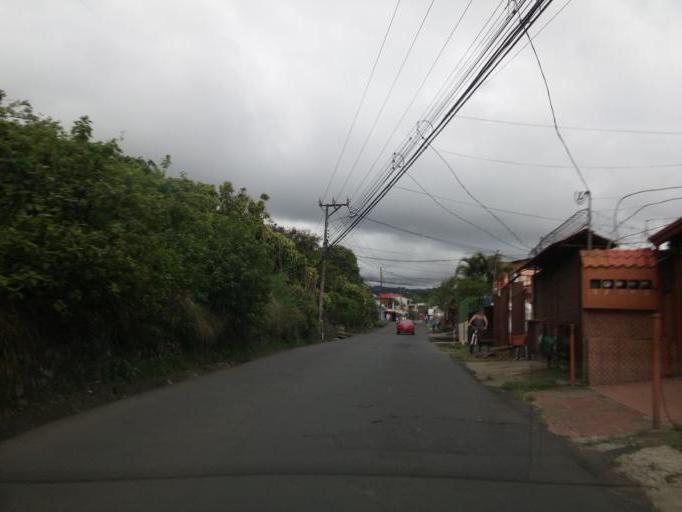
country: CR
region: Heredia
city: Santo Domingo
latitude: 10.0390
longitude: -84.1514
